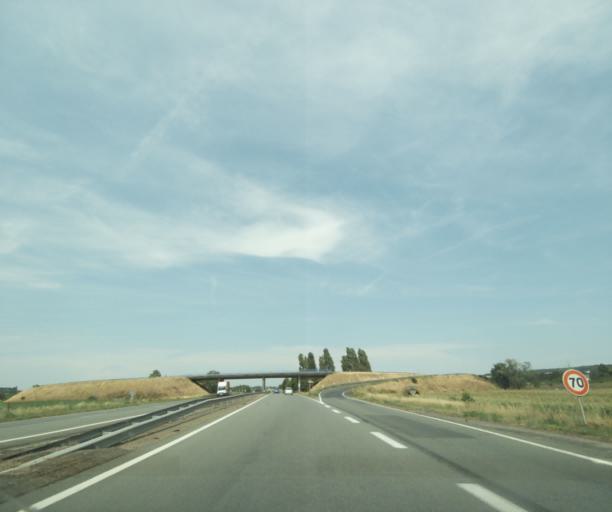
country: FR
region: Poitou-Charentes
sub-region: Departement de la Vienne
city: Dange-Saint-Romain
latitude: 46.8970
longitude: 0.5715
